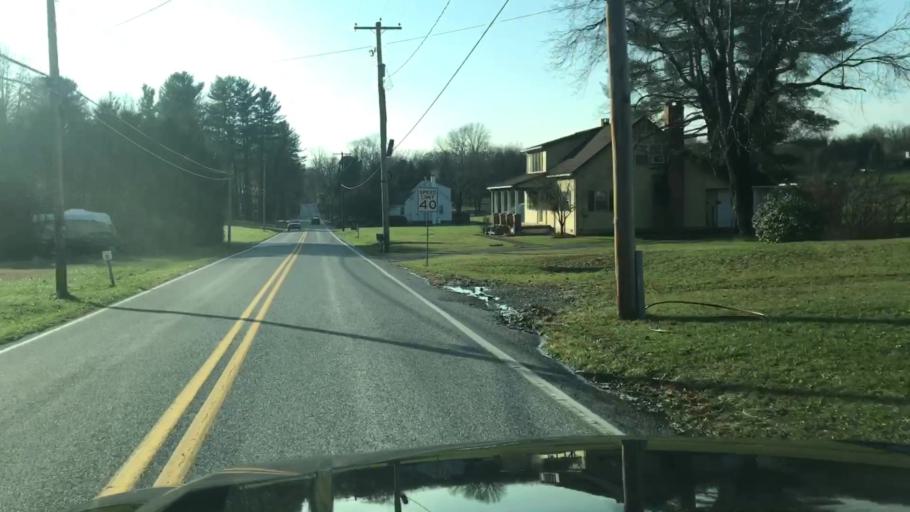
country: US
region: Pennsylvania
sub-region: Cumberland County
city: Lower Allen
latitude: 40.1695
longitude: -76.8973
